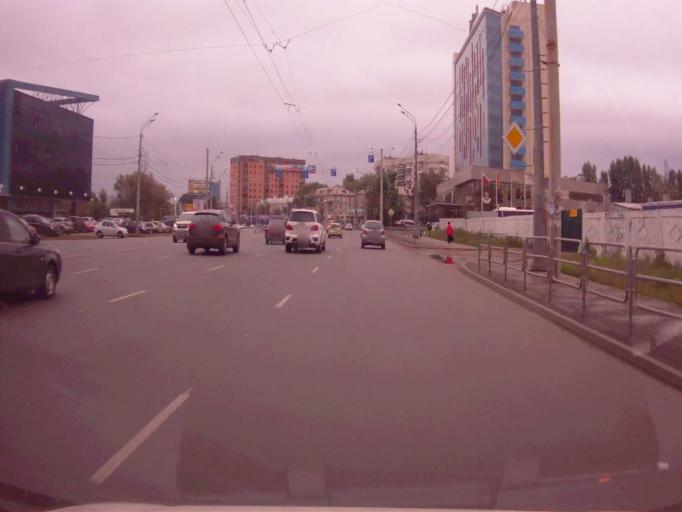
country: RU
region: Chelyabinsk
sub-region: Gorod Chelyabinsk
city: Chelyabinsk
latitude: 55.1655
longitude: 61.3807
